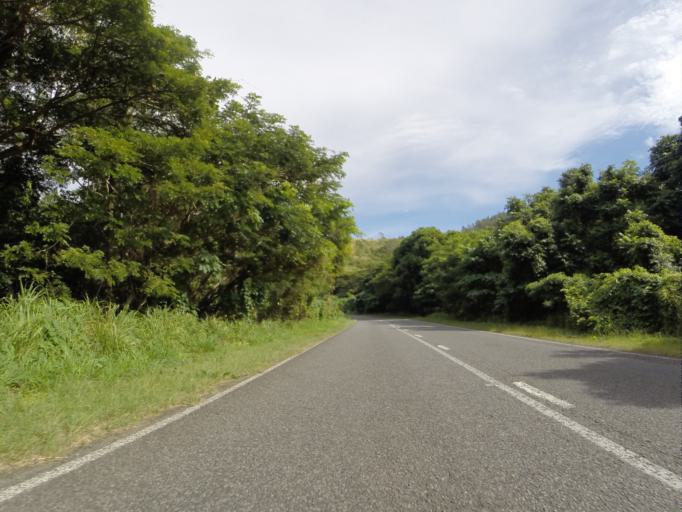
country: FJ
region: Western
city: Nadi
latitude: -18.1926
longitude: 177.6363
